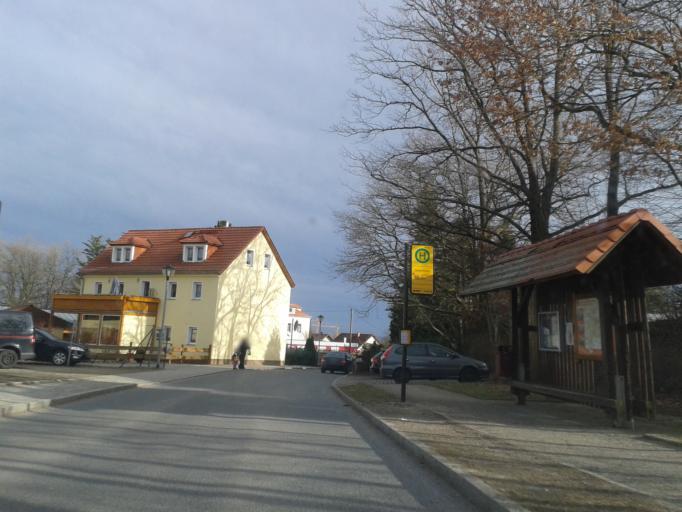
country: DE
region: Saxony
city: Freital
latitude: 51.0294
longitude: 13.6487
